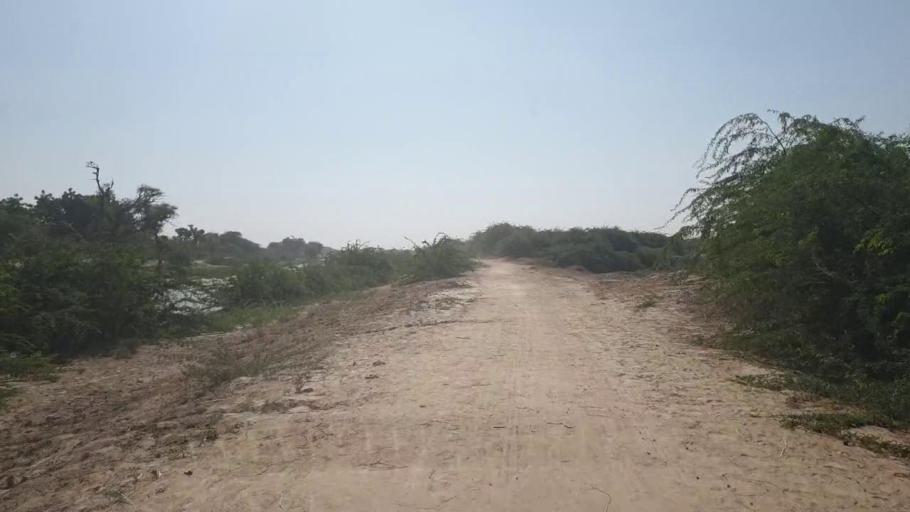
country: PK
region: Sindh
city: Talhar
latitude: 24.8213
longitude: 68.7937
